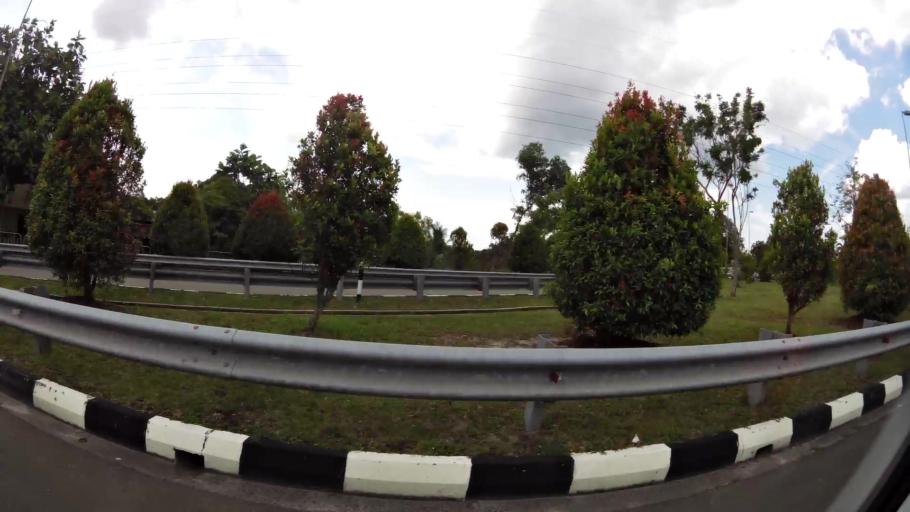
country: BN
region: Brunei and Muara
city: Bandar Seri Begawan
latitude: 4.9495
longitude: 114.9627
